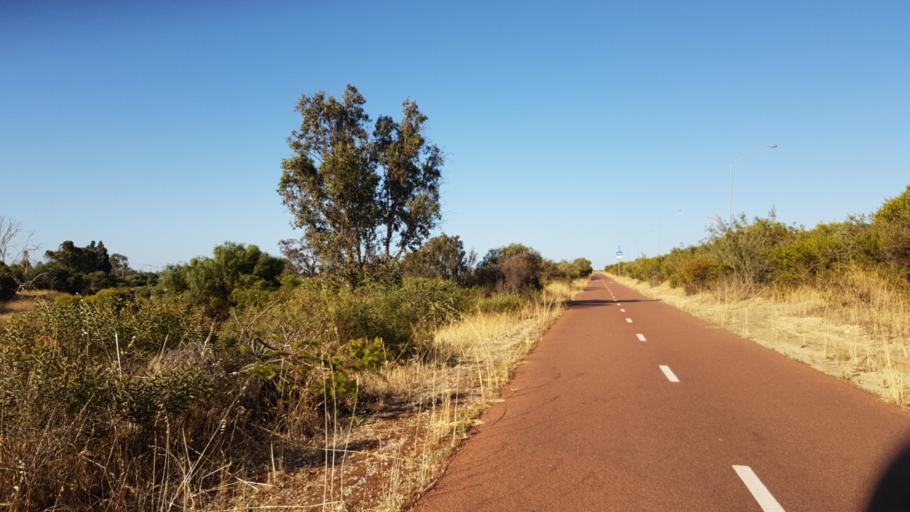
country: AU
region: Western Australia
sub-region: Kwinana
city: Wellard
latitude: -32.2743
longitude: 115.8422
